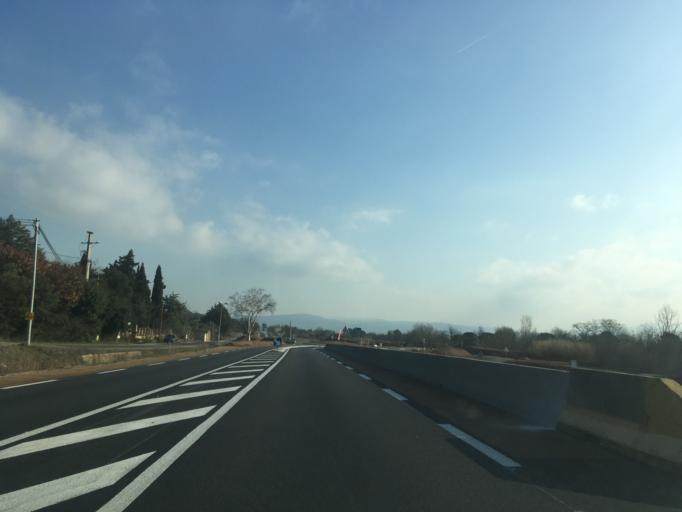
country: FR
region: Provence-Alpes-Cote d'Azur
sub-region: Departement du Var
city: Vidauban
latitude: 43.4034
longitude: 6.3909
